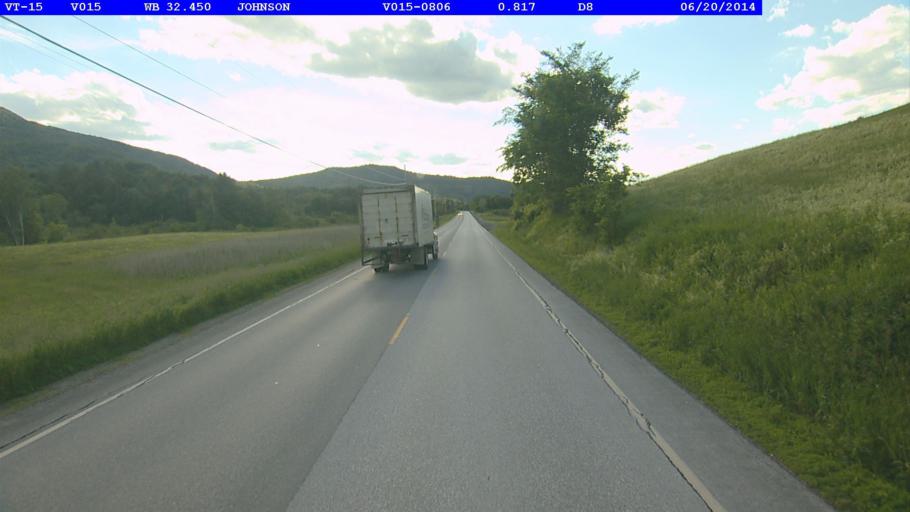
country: US
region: Vermont
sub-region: Lamoille County
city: Johnson
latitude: 44.6476
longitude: -72.7387
